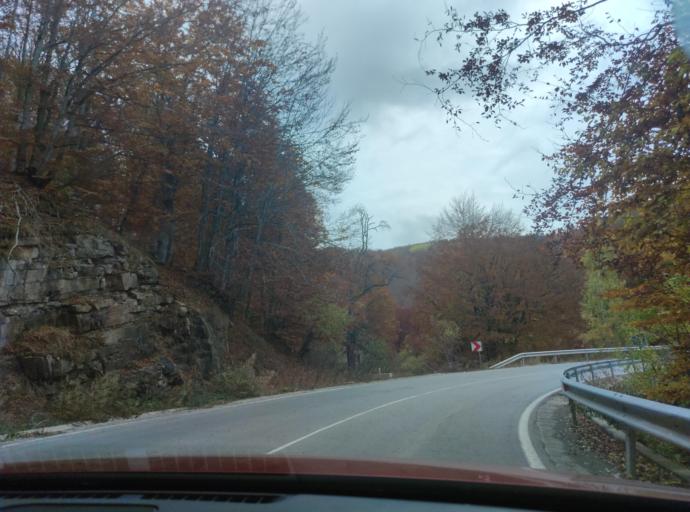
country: BG
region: Sofiya
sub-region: Obshtina Godech
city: Godech
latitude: 43.1093
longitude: 23.1057
